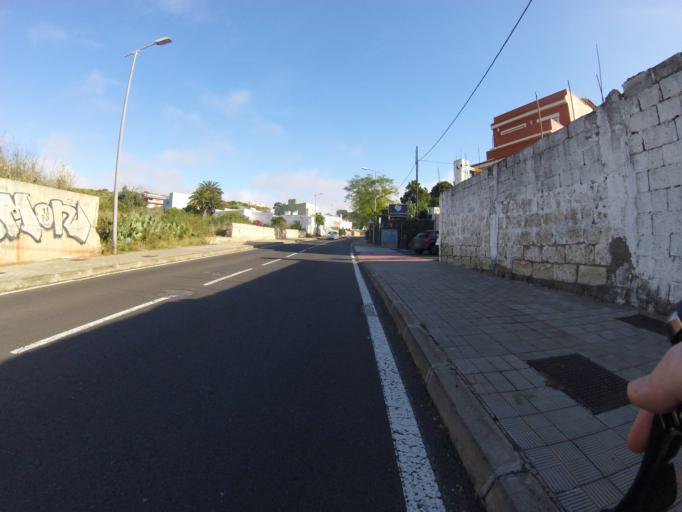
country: ES
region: Canary Islands
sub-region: Provincia de Santa Cruz de Tenerife
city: La Laguna
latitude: 28.4671
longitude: -16.3169
